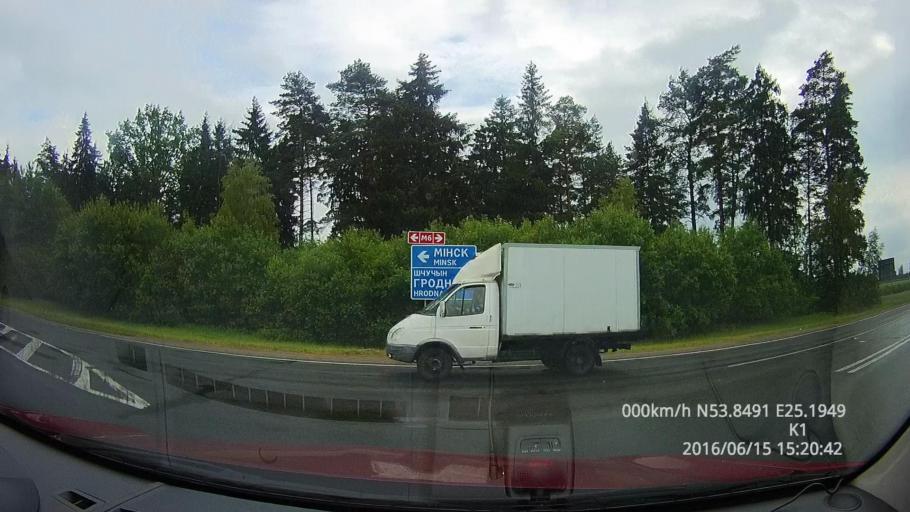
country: BY
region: Grodnenskaya
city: Lida
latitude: 53.8490
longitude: 25.1953
